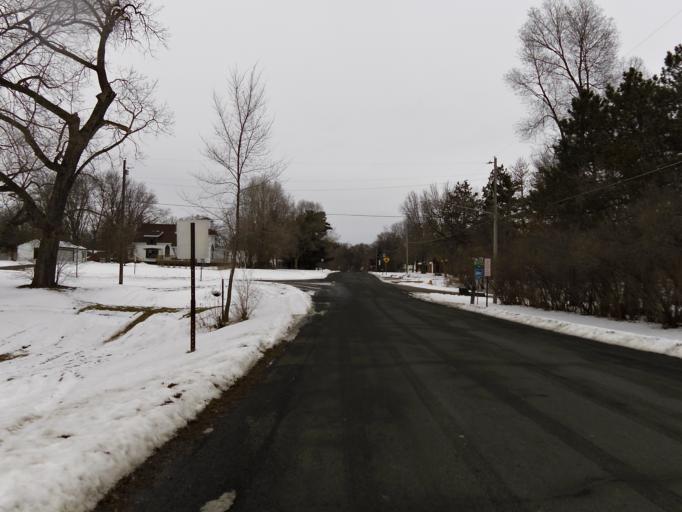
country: US
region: Minnesota
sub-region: Washington County
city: Lakeland
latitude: 44.9592
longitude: -92.7673
